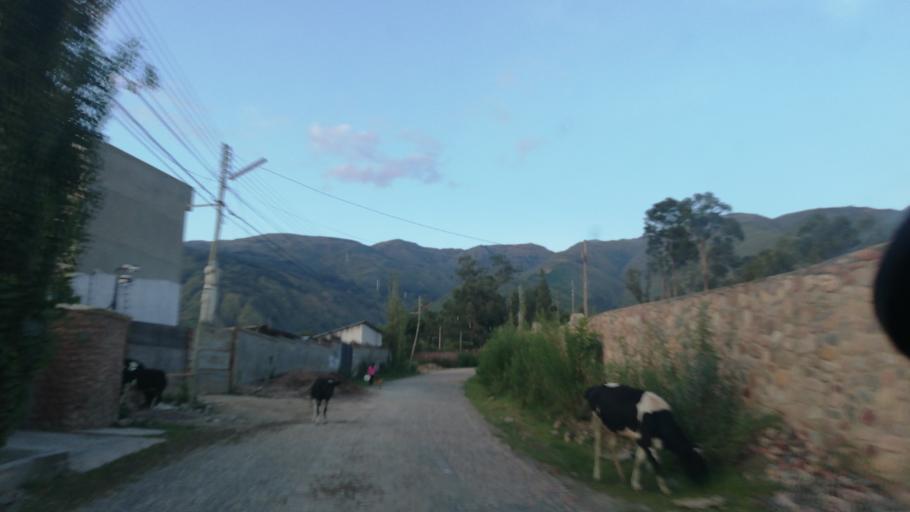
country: BO
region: Cochabamba
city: Cochabamba
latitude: -17.3362
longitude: -66.2099
